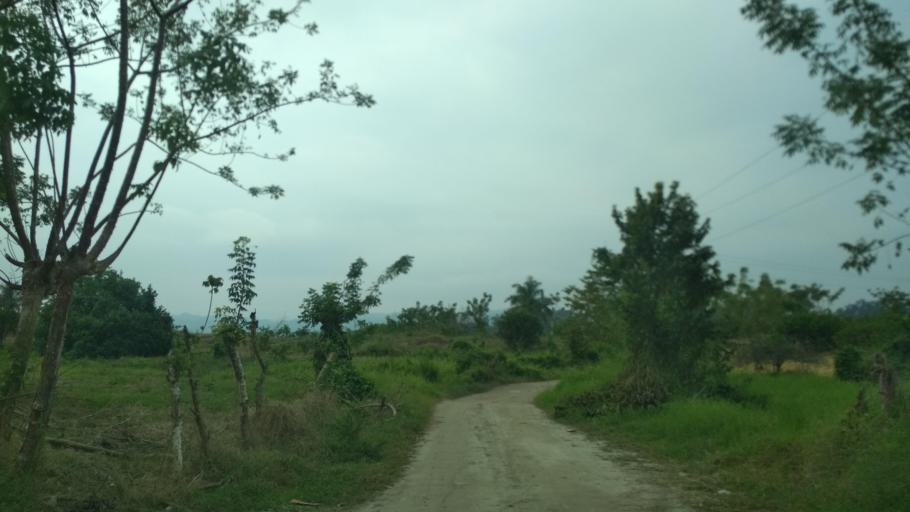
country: MM
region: Kayah
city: Loikaw
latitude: 20.2172
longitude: 97.3322
